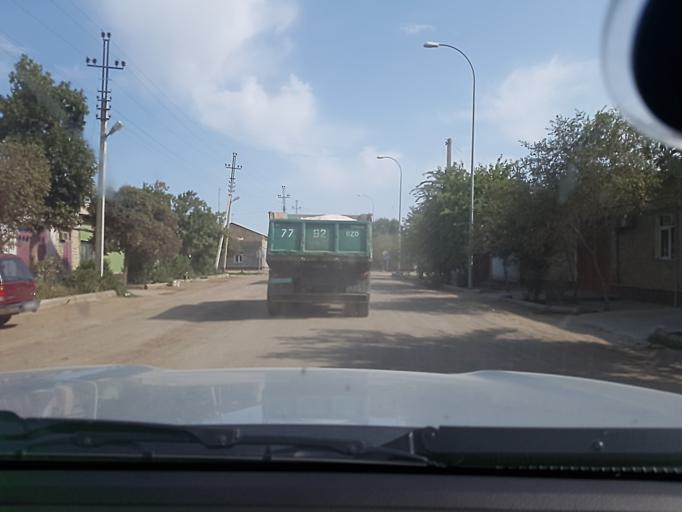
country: TM
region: Dasoguz
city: Dasoguz
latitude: 41.8268
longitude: 59.9794
